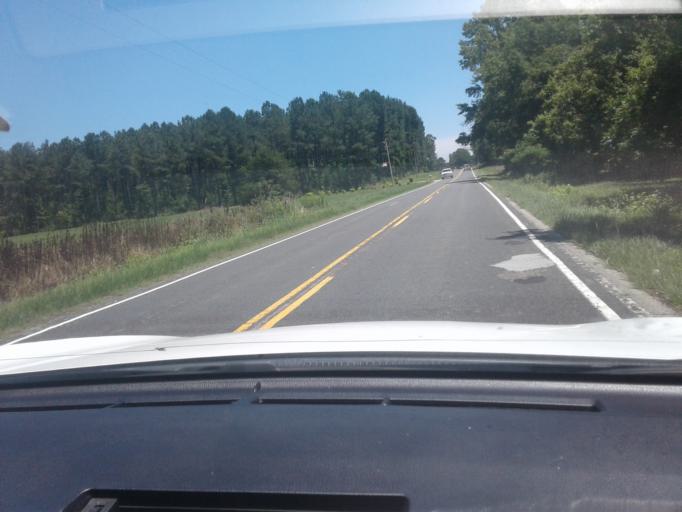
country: US
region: North Carolina
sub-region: Harnett County
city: Lillington
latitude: 35.3899
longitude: -78.7830
